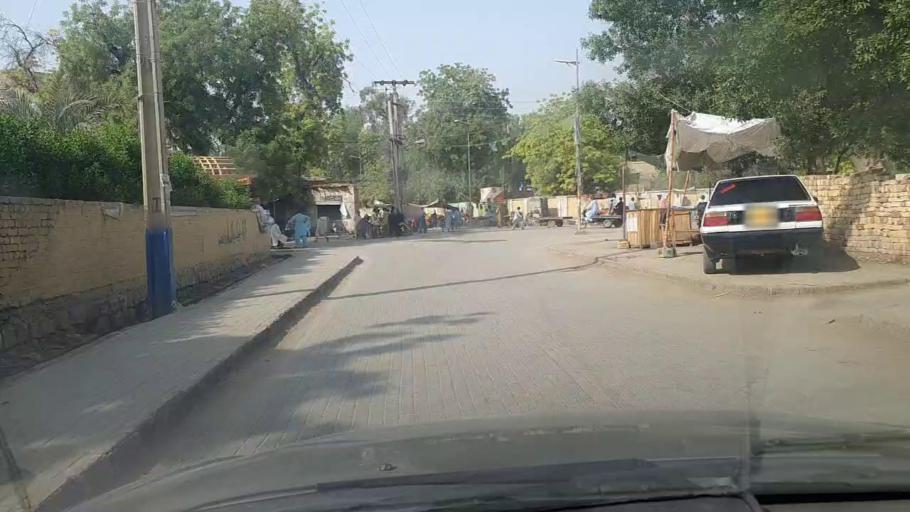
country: PK
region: Sindh
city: Mirpur Mathelo
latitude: 28.0214
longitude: 69.5520
